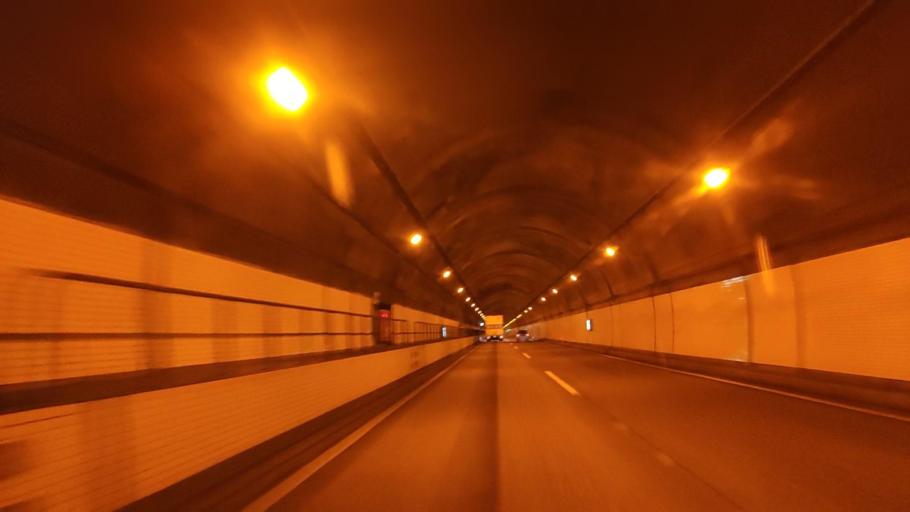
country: JP
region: Niigata
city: Itoigawa
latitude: 37.0614
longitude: 137.9313
